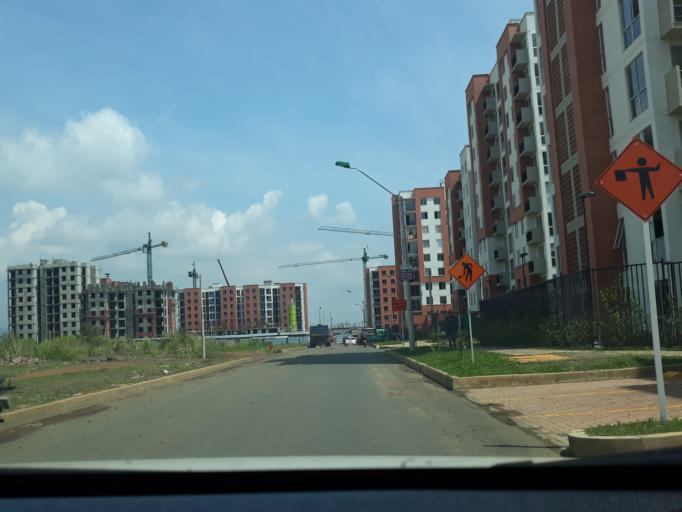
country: CO
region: Valle del Cauca
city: Cali
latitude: 3.3698
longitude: -76.5058
